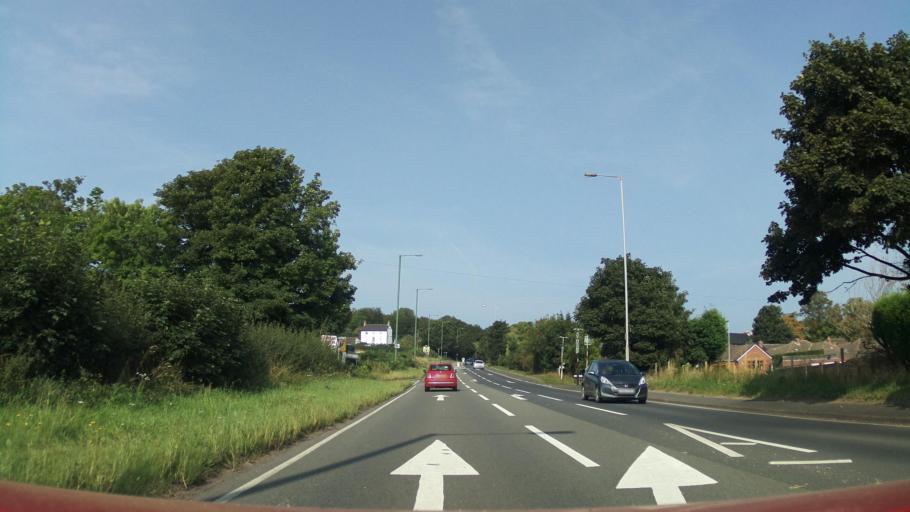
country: GB
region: England
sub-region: Walsall
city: Aldridge
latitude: 52.6265
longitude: -1.9018
